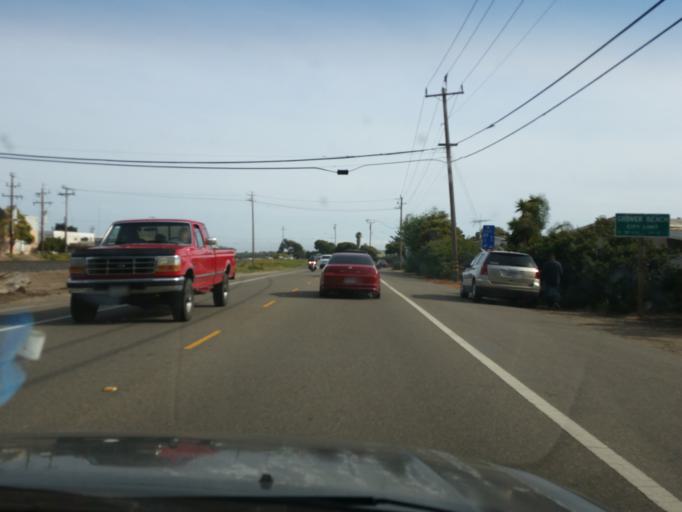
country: US
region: California
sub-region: San Luis Obispo County
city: Grover Beach
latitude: 35.1284
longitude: -120.6319
